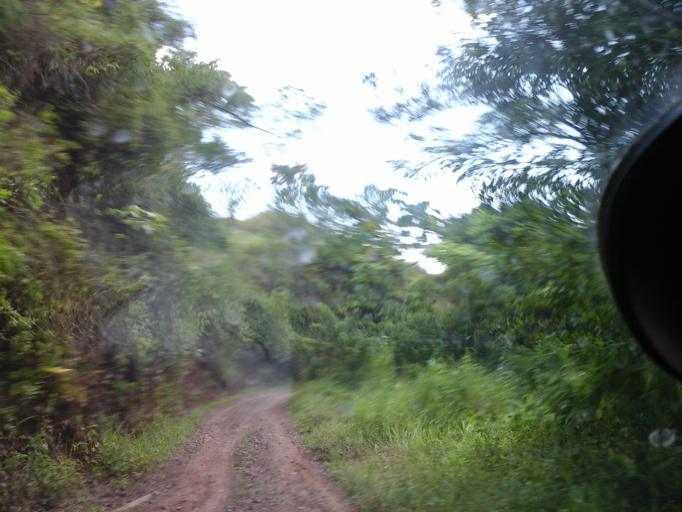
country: CO
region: Cesar
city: San Diego
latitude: 10.2710
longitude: -73.0895
